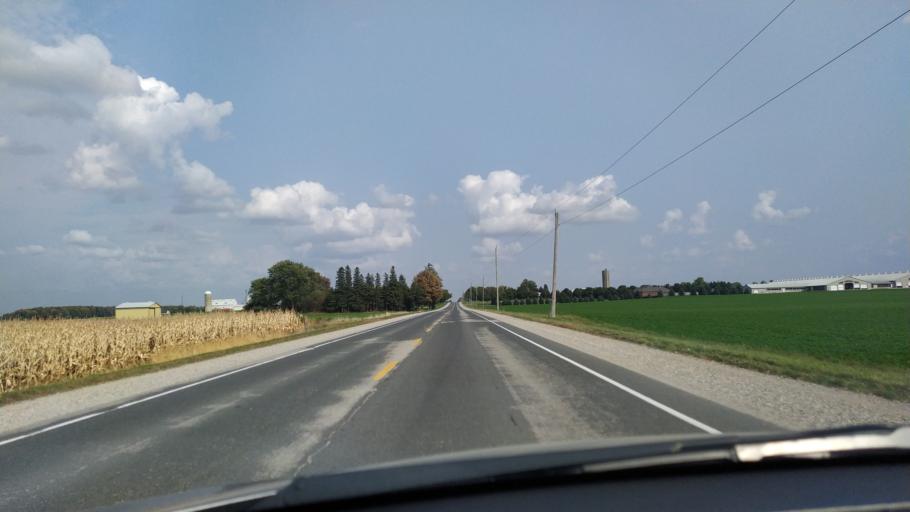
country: CA
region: Ontario
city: Stratford
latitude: 43.3513
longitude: -80.8526
